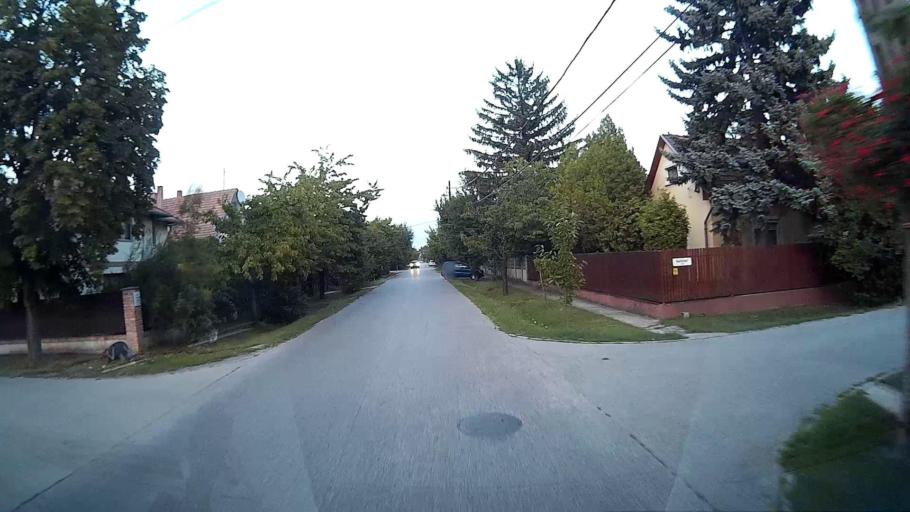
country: HU
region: Pest
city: Budakalasz
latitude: 47.6315
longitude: 19.0564
